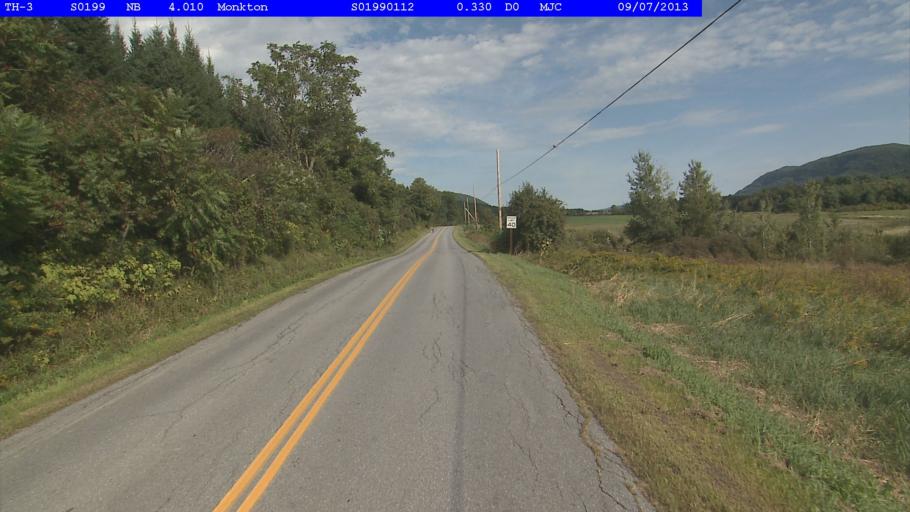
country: US
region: Vermont
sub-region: Addison County
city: Bristol
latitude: 44.1854
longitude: -73.1065
